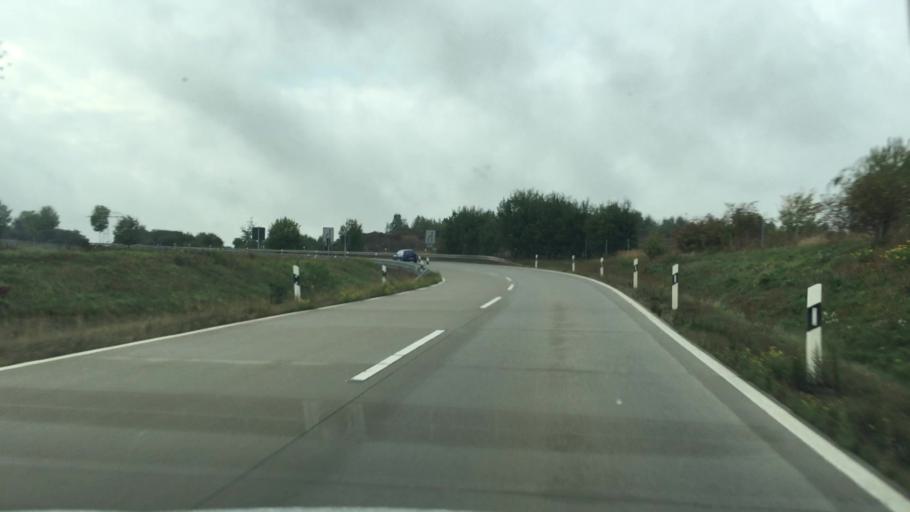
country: DE
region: Saxony
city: Wittgensdorf
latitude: 50.8524
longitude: 12.8433
